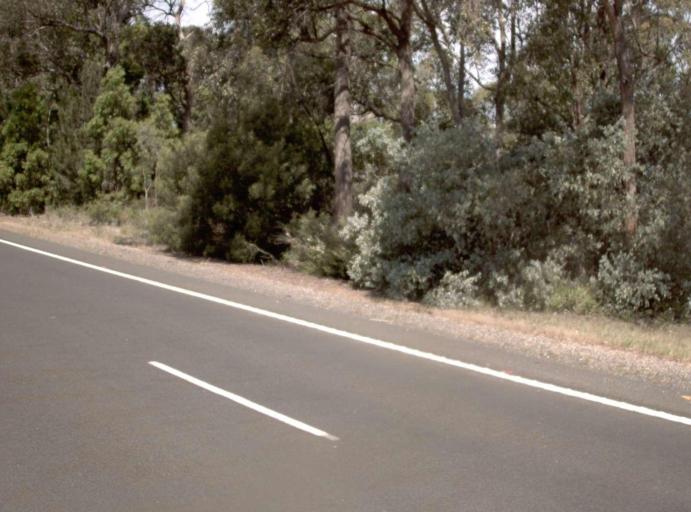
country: AU
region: Victoria
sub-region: Wellington
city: Sale
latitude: -37.9127
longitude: 147.3071
